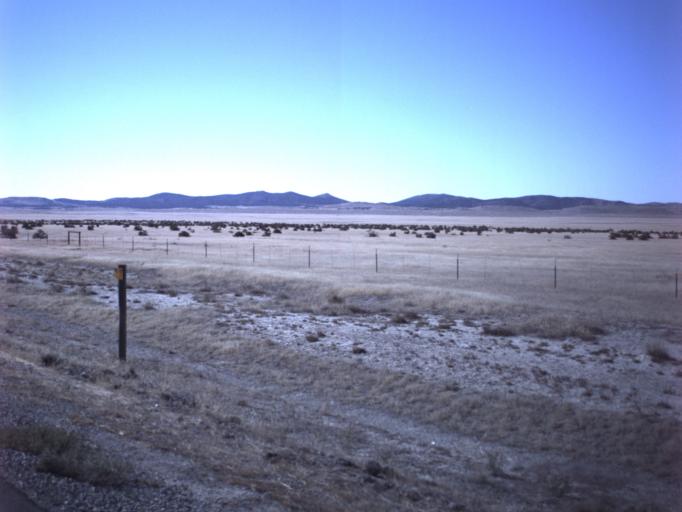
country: US
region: Utah
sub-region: Tooele County
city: Grantsville
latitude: 40.3187
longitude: -112.7437
